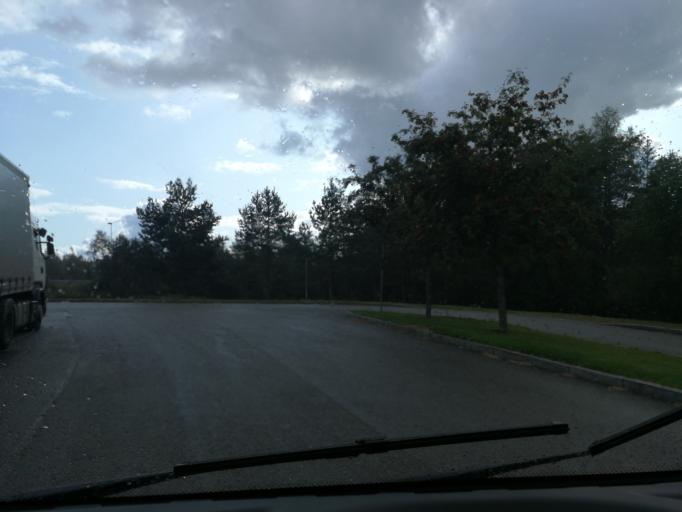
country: NO
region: Ostfold
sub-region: Marker
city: Orje
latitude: 59.5410
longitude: 11.5383
